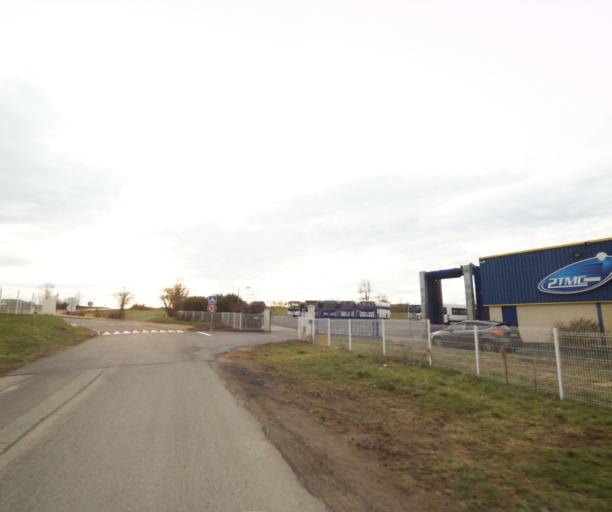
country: FR
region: Rhone-Alpes
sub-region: Departement de la Loire
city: Sury-le-Comtal
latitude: 45.5240
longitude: 4.1875
